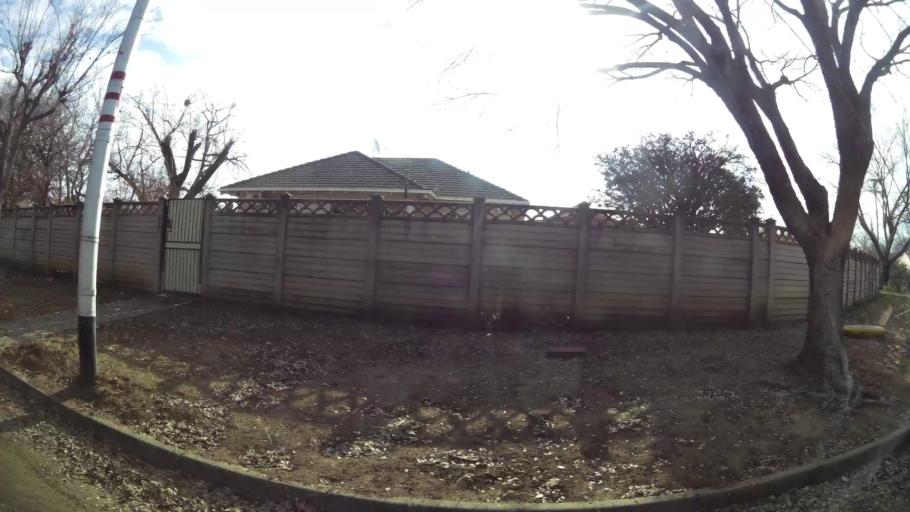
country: ZA
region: Orange Free State
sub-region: Mangaung Metropolitan Municipality
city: Bloemfontein
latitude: -29.0754
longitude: 26.2395
